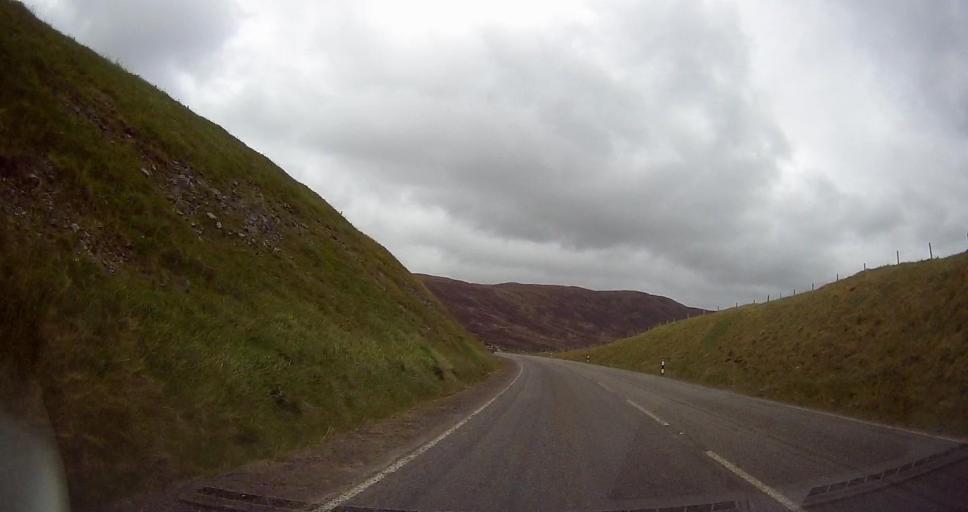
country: GB
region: Scotland
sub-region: Shetland Islands
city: Lerwick
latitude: 60.3709
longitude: -1.3133
